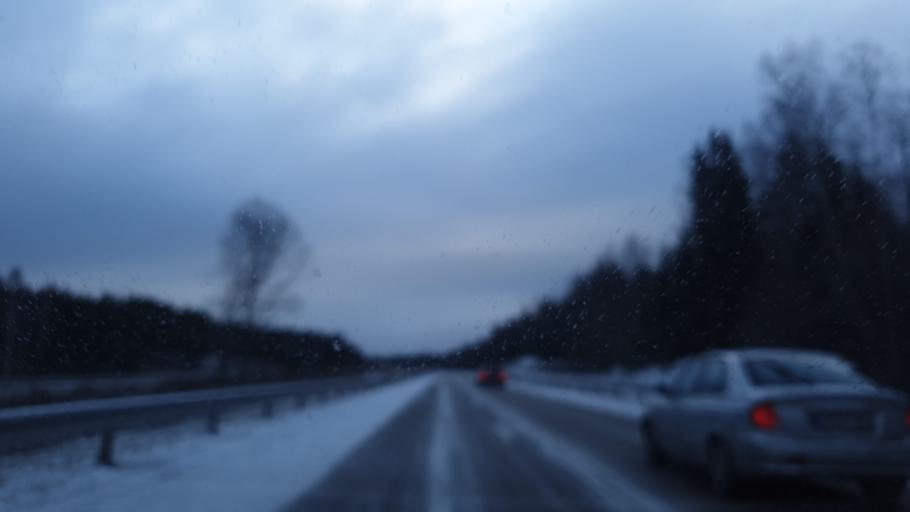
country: SE
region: Uppsala
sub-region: Alvkarleby Kommun
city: AElvkarleby
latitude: 60.4357
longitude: 17.3351
